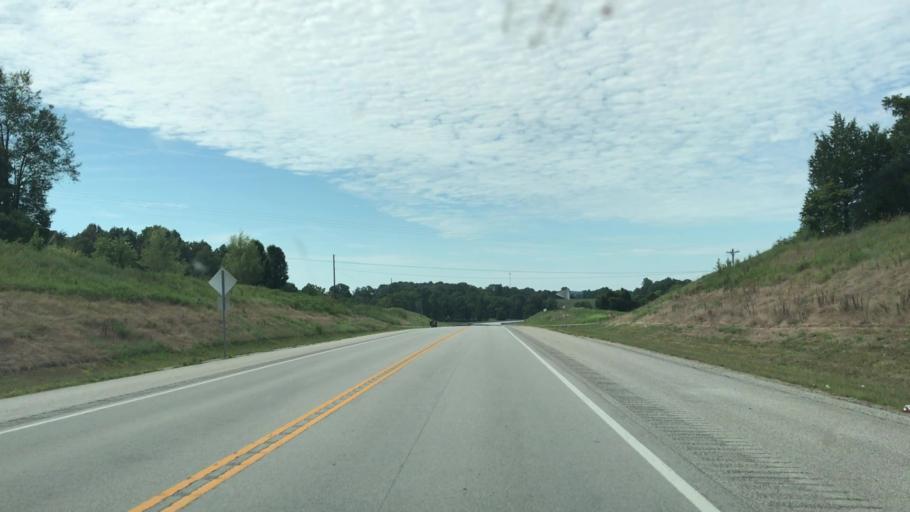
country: US
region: Kentucky
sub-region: Edmonson County
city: Brownsville
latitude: 37.1538
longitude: -86.2214
